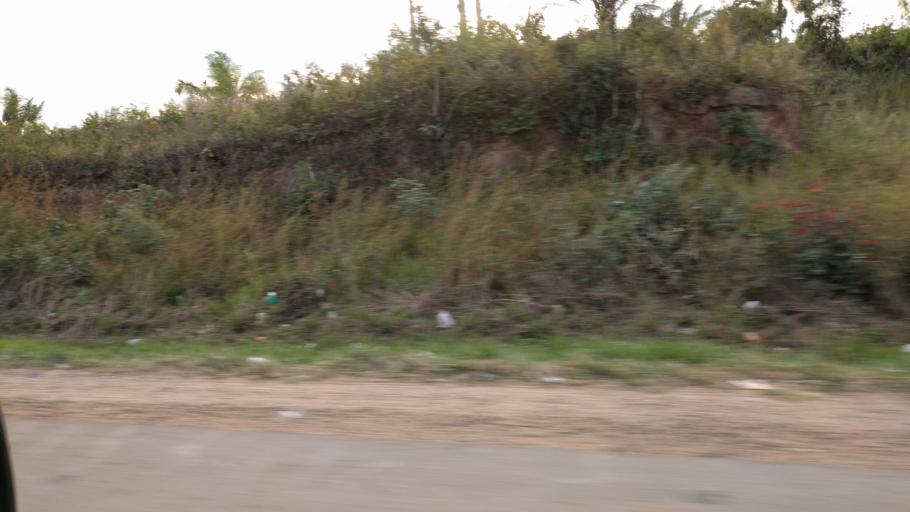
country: BO
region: Santa Cruz
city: Buena Vista
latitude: -17.4400
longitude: -63.6438
